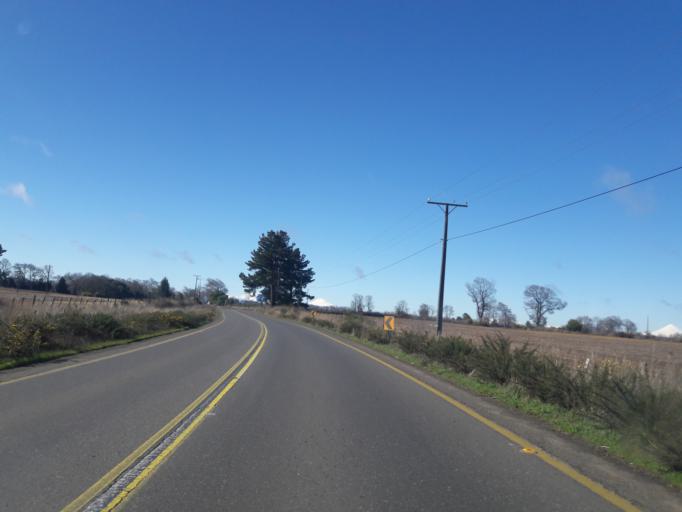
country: CL
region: Araucania
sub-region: Provincia de Malleco
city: Victoria
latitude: -38.2536
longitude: -72.2914
